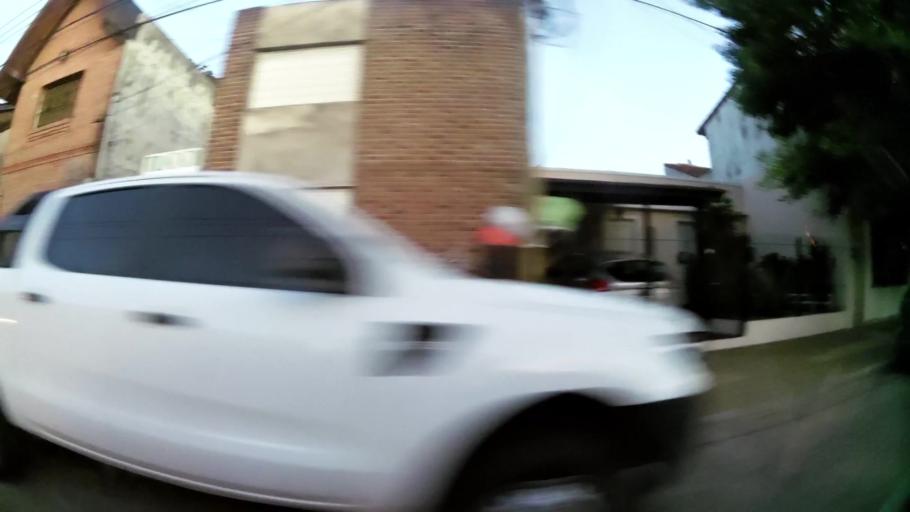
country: AR
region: Buenos Aires
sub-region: Partido de Moron
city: Moron
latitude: -34.6581
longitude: -58.6329
